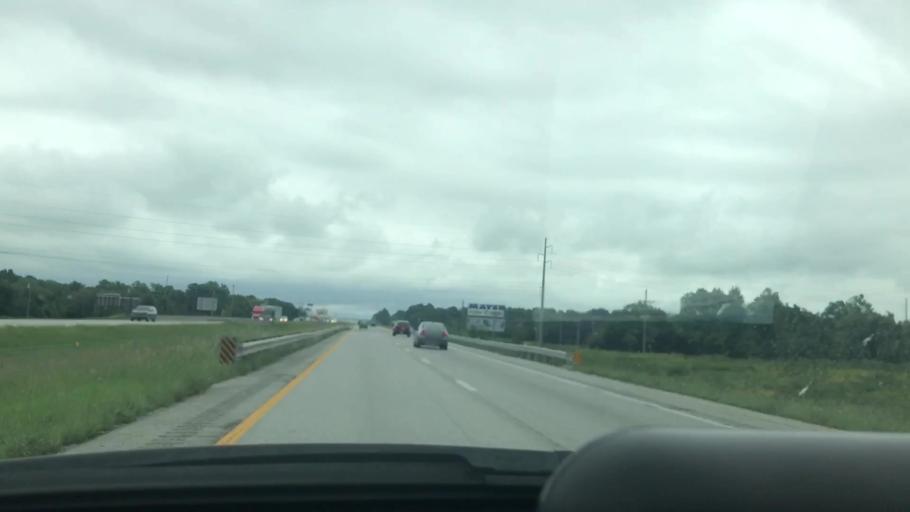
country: US
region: Missouri
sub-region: Jasper County
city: Duquesne
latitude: 37.0489
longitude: -94.4637
